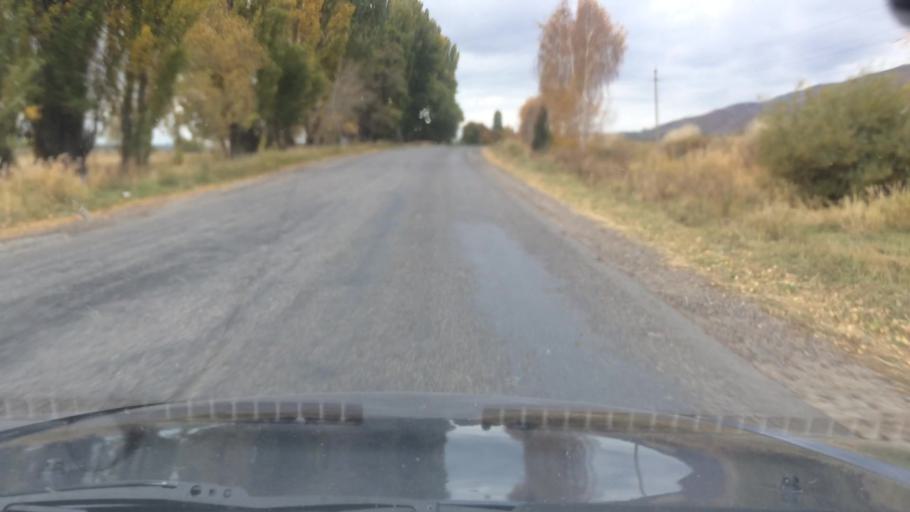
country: KG
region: Ysyk-Koel
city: Tyup
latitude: 42.7632
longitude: 78.1716
